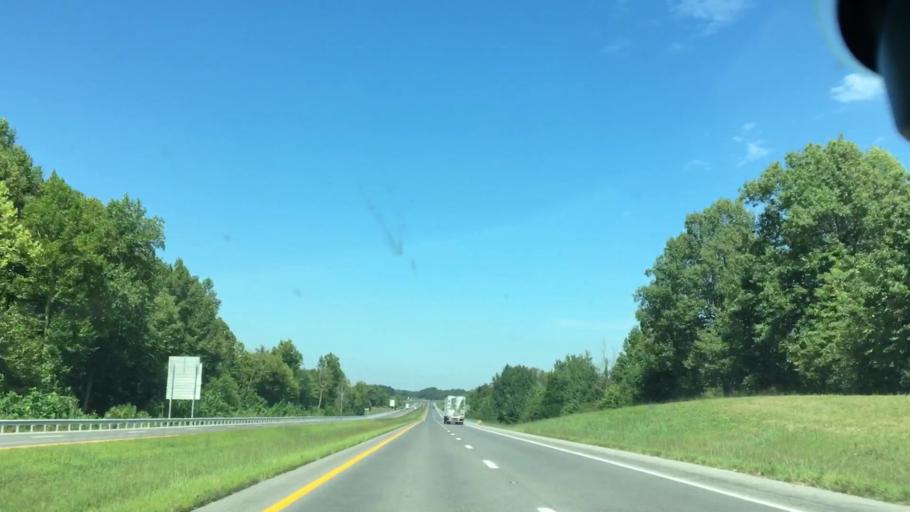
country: US
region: Kentucky
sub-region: Webster County
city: Sebree
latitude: 37.5002
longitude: -87.4751
